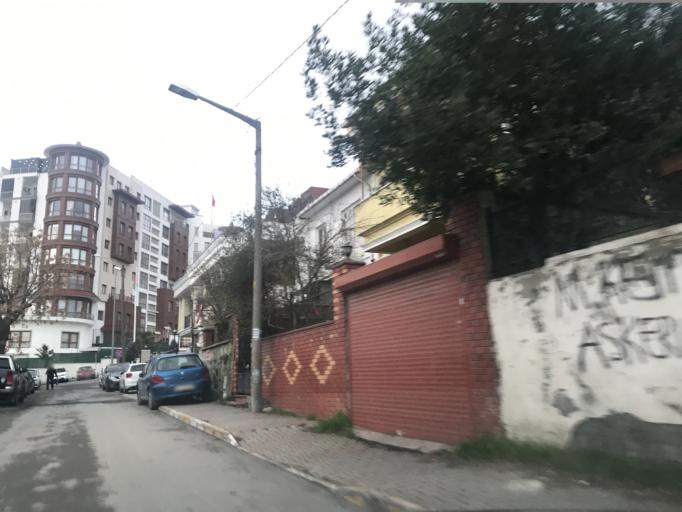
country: TR
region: Istanbul
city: Istanbul
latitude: 41.0400
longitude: 28.9238
